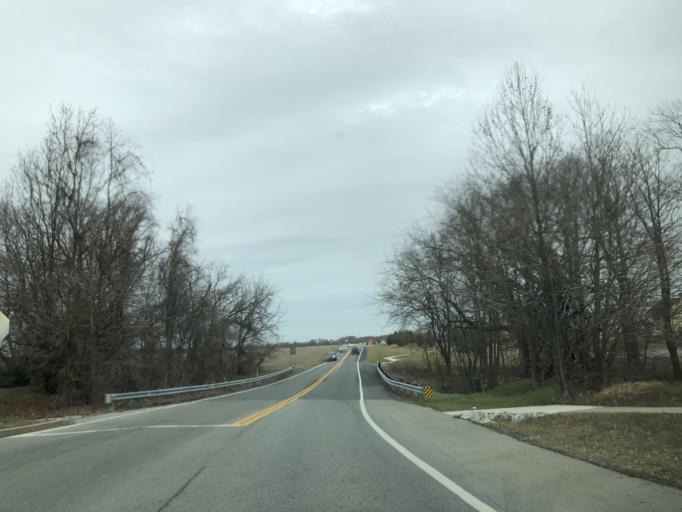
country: US
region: Delaware
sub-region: New Castle County
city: Middletown
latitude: 39.4715
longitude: -75.7088
